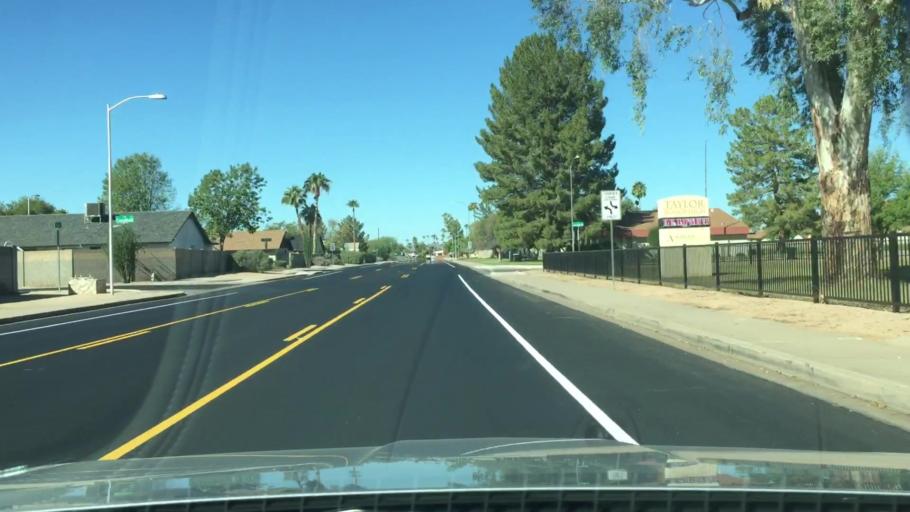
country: US
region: Arizona
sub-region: Maricopa County
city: Gilbert
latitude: 33.4039
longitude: -111.7624
